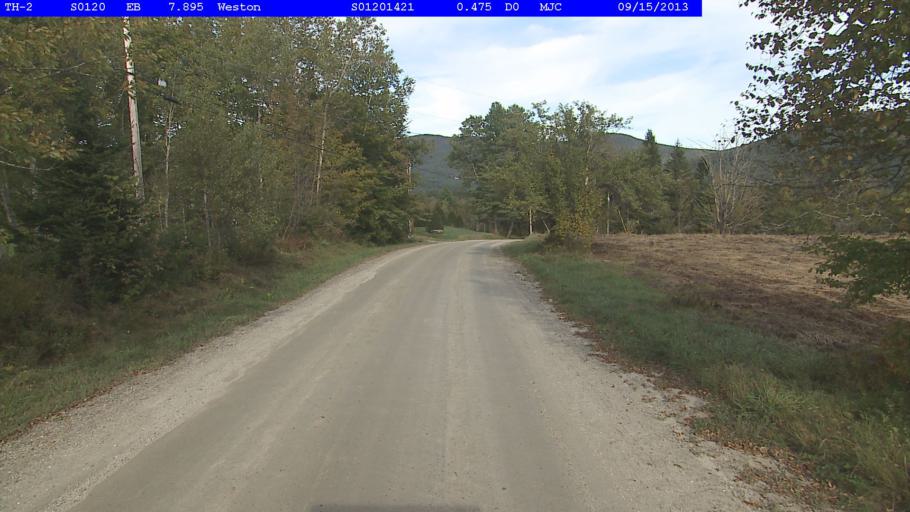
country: US
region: Vermont
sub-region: Windsor County
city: Chester
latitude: 43.2900
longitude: -72.8104
